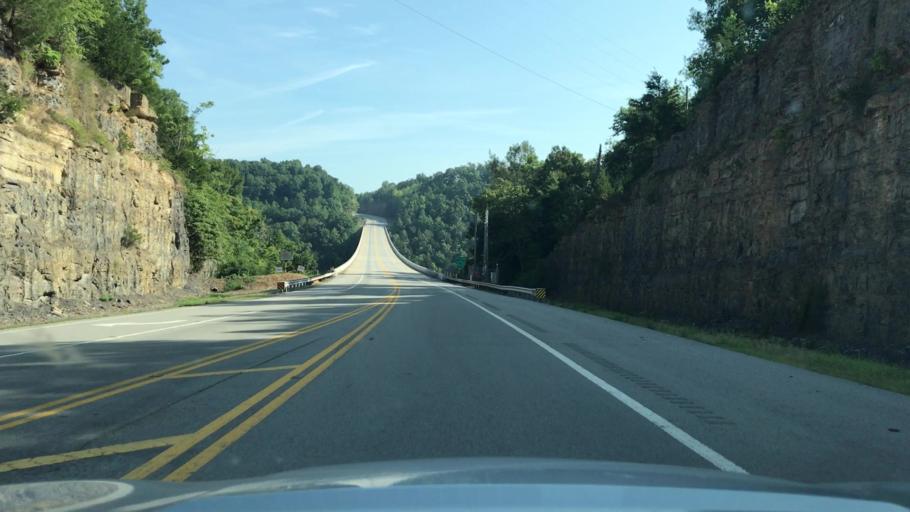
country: US
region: Tennessee
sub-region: Pickett County
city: Byrdstown
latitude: 36.5303
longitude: -85.1619
